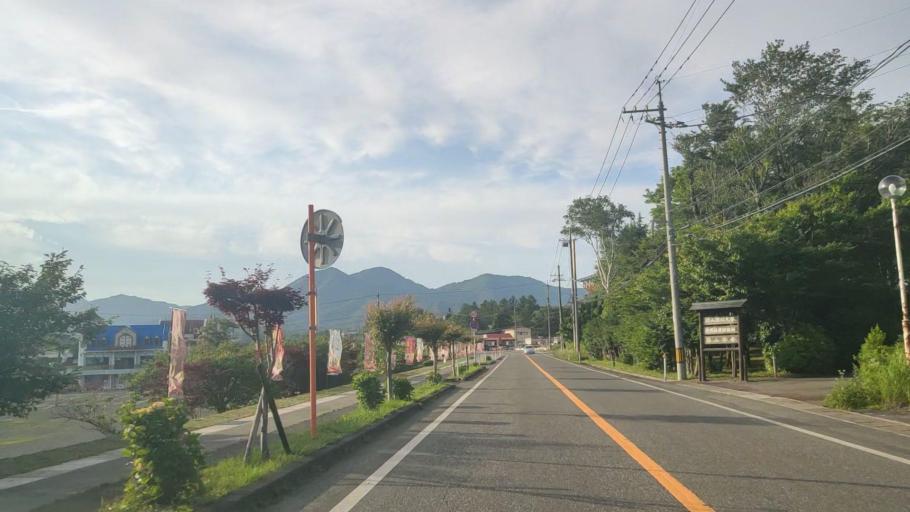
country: JP
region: Tottori
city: Kurayoshi
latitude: 35.2896
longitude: 133.6366
